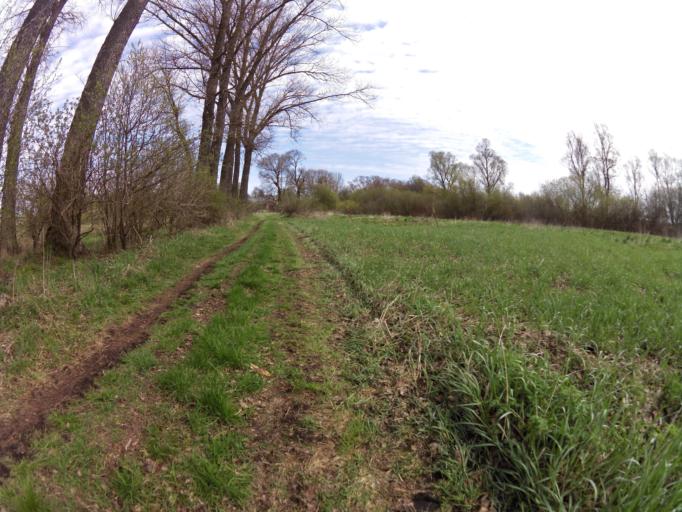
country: PL
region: West Pomeranian Voivodeship
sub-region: Powiat szczecinecki
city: Borne Sulinowo
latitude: 53.7065
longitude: 16.5389
